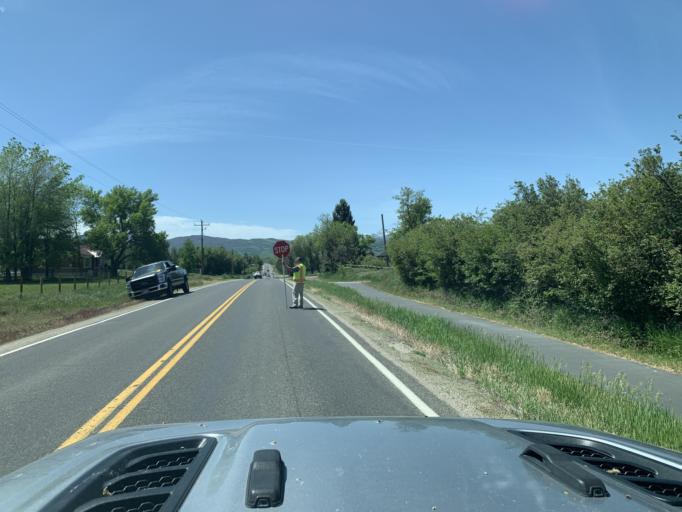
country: US
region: Utah
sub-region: Weber County
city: Wolf Creek
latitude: 41.2842
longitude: -111.7771
